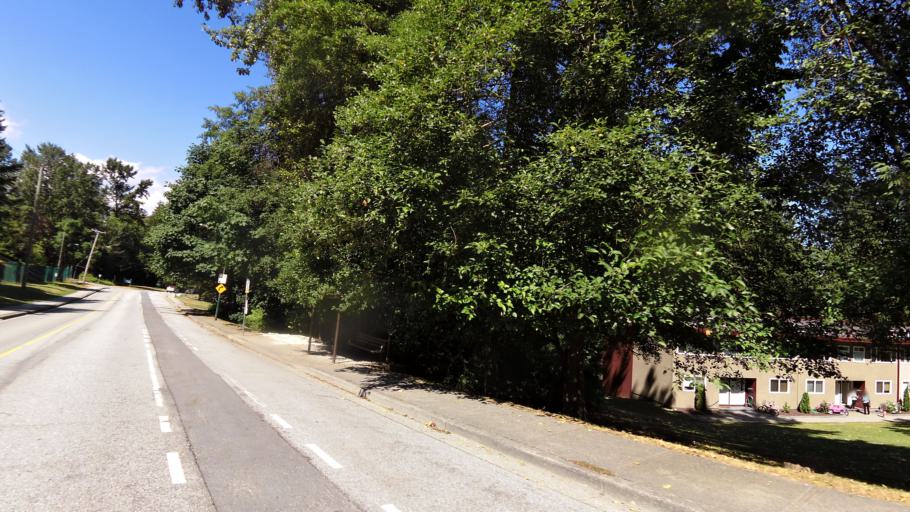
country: CA
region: British Columbia
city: Port Moody
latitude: 49.2789
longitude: -122.8809
